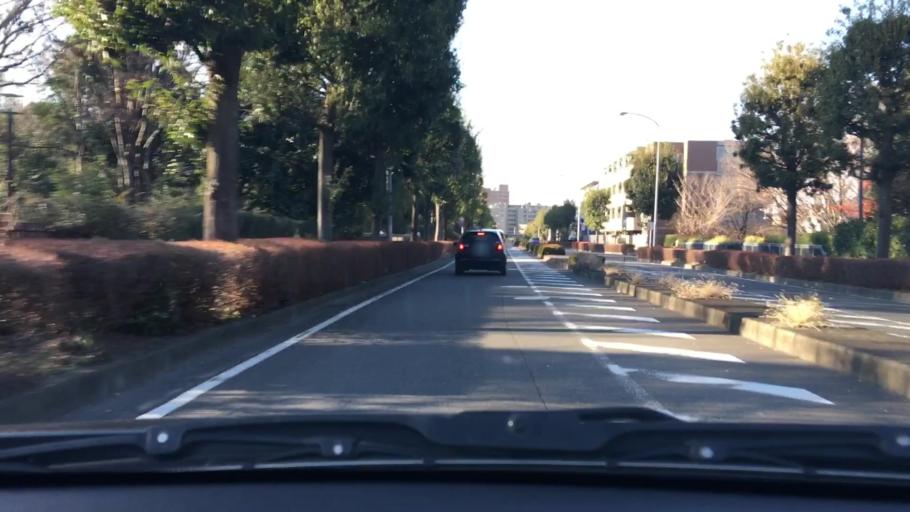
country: JP
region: Kanagawa
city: Yokohama
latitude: 35.5380
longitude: 139.5919
